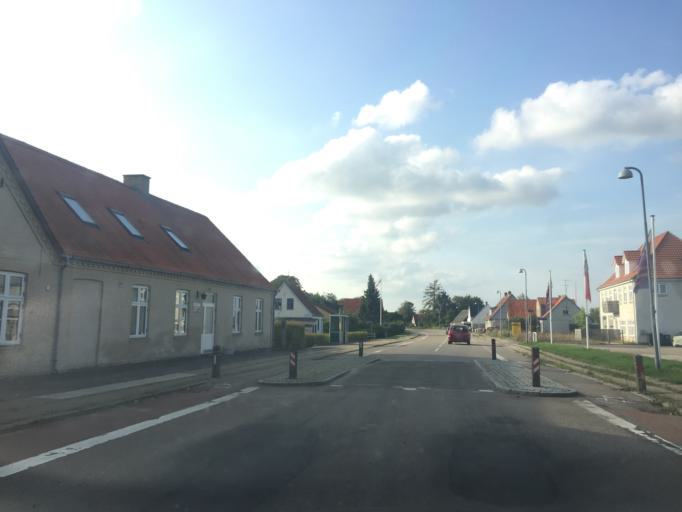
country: DK
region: Zealand
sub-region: Kalundborg Kommune
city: Svebolle
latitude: 55.6618
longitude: 11.2672
